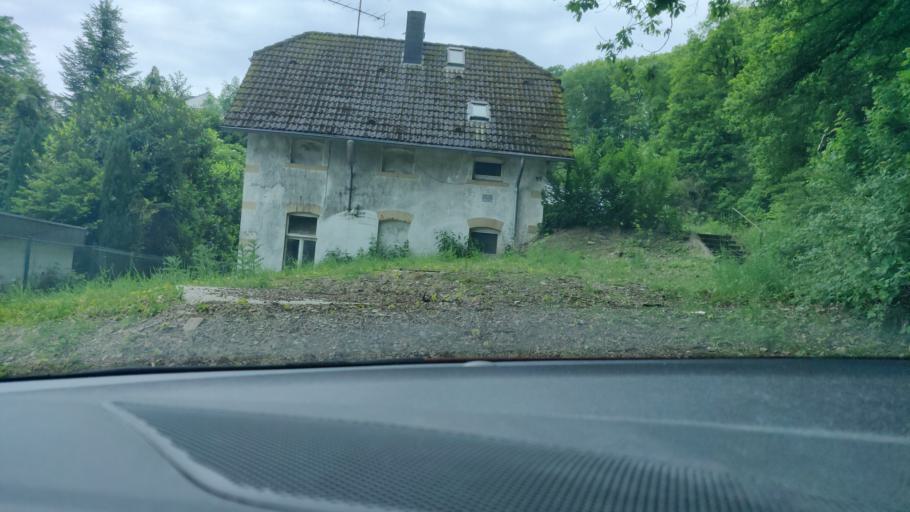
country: DE
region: North Rhine-Westphalia
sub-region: Regierungsbezirk Dusseldorf
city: Velbert
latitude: 51.3106
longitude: 7.0786
